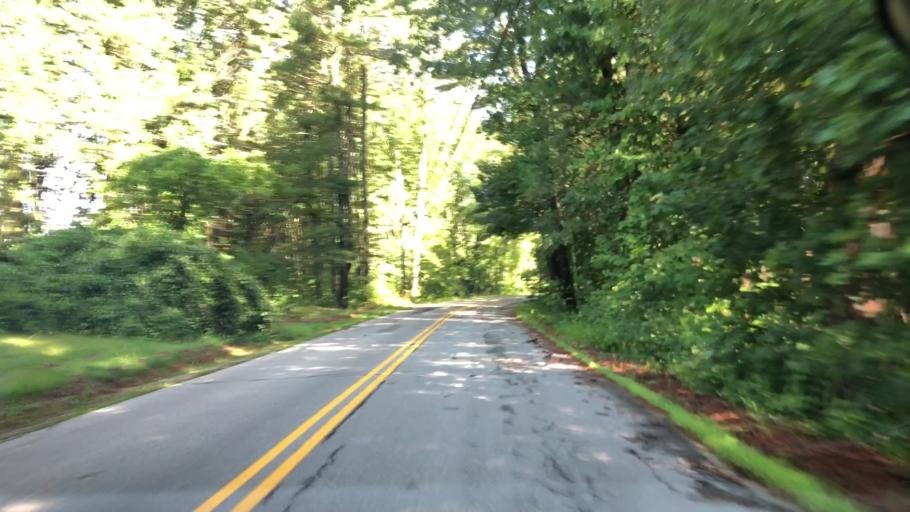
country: US
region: New Hampshire
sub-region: Hillsborough County
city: Milford
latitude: 42.8375
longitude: -71.5948
